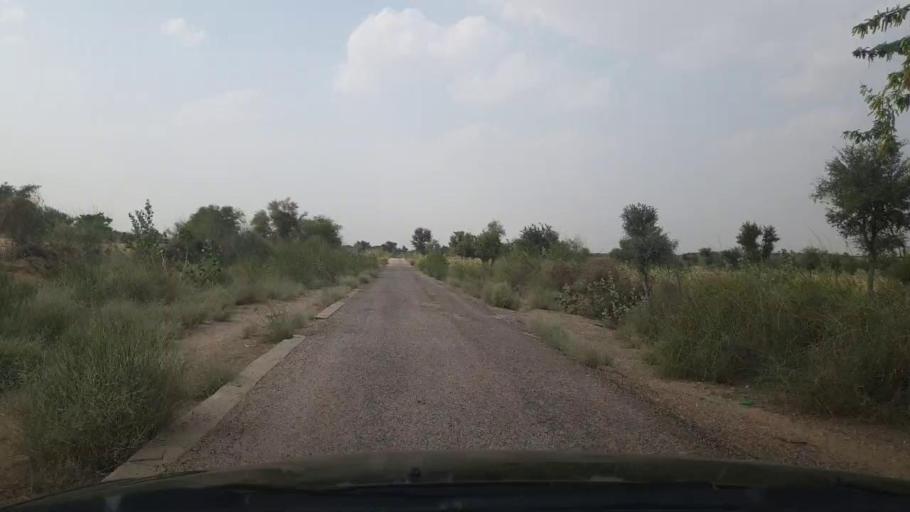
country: PK
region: Sindh
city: Islamkot
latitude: 24.9796
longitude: 70.5834
